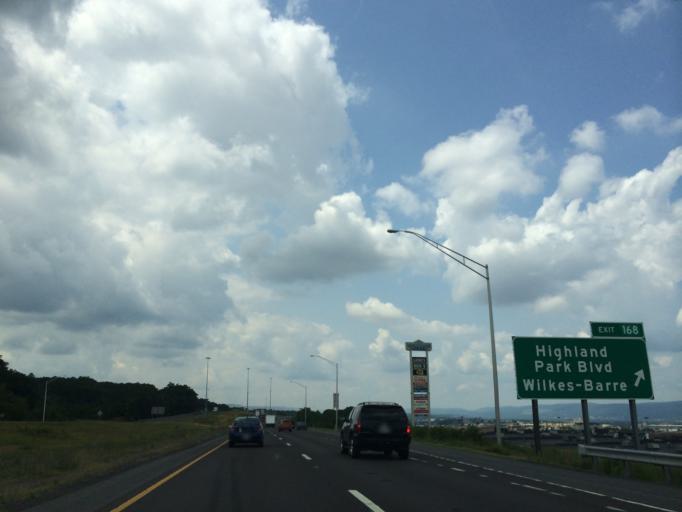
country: US
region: Pennsylvania
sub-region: Luzerne County
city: Georgetown
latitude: 41.2387
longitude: -75.8381
